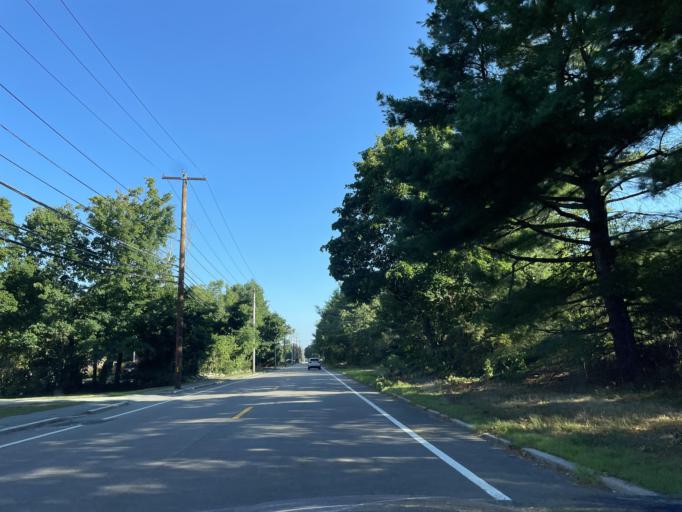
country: US
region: Massachusetts
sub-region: Norfolk County
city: Foxborough
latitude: 42.0486
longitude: -71.2357
